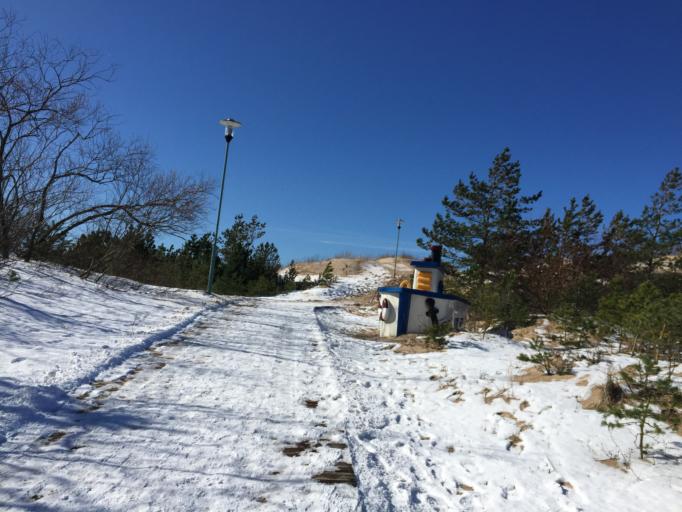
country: LV
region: Ventspils
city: Ventspils
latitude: 57.3920
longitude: 21.5320
